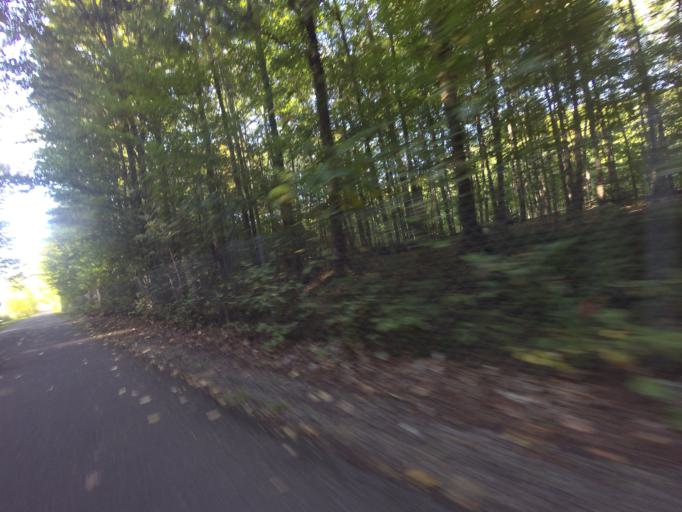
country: CA
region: Quebec
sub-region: Laurentides
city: Saint-Jerome
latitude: 45.7432
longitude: -73.9614
